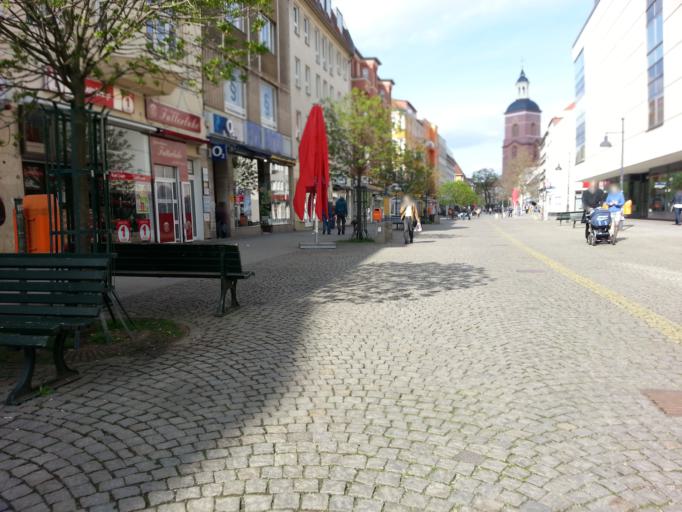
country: DE
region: Berlin
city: Spandau
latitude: 52.5364
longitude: 13.2022
